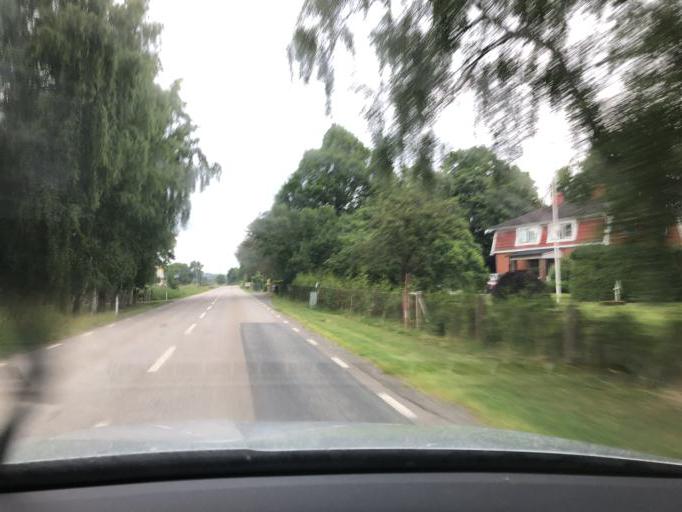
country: SE
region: Blekinge
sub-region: Solvesborgs Kommun
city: Soelvesborg
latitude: 56.1034
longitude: 14.6184
